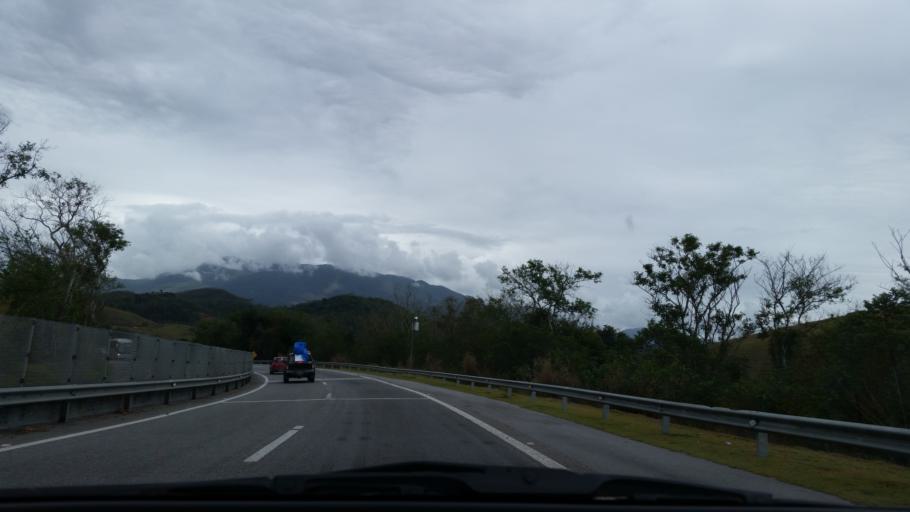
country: BR
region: Rio de Janeiro
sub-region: Rio Bonito
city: Rio Bonito
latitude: -22.7440
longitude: -42.5969
